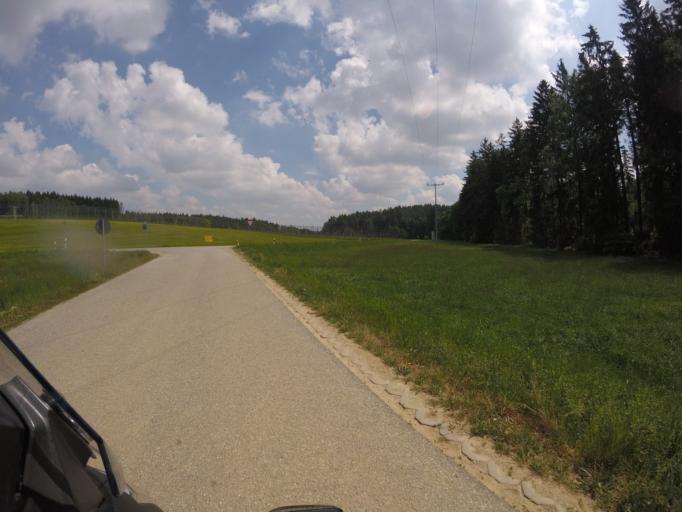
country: DE
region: Bavaria
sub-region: Lower Bavaria
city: Attenhofen
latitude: 48.6411
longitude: 11.8589
